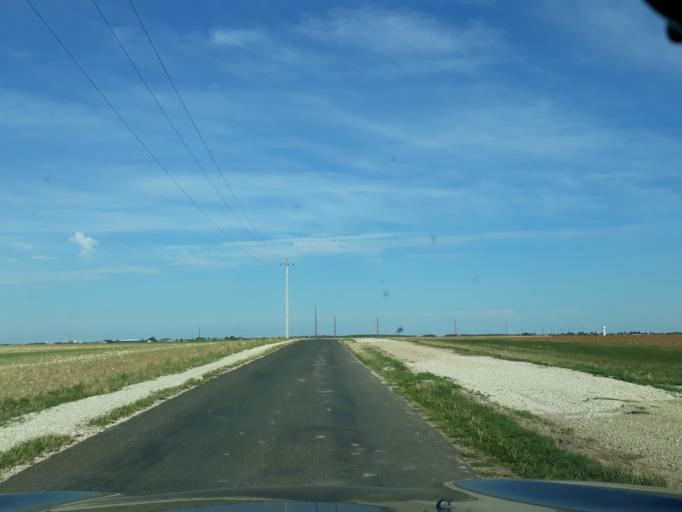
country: FR
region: Centre
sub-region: Departement du Loir-et-Cher
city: Ouzouer-le-Marche
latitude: 47.9386
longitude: 1.5420
